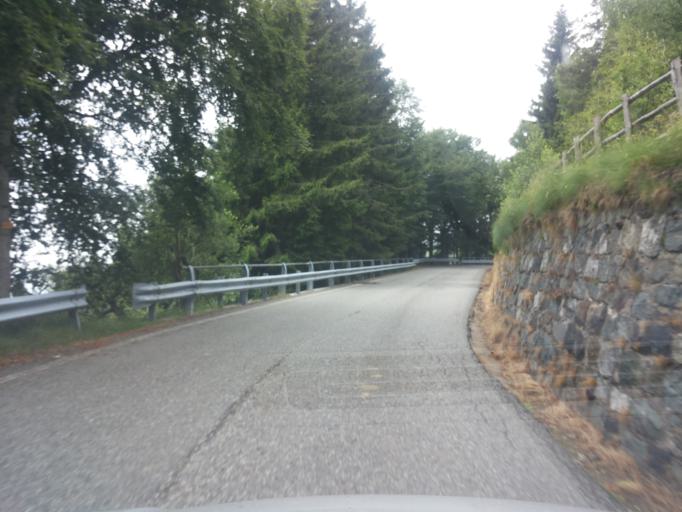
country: IT
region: Piedmont
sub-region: Provincia di Biella
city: Camandona
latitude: 45.6624
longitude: 8.0797
